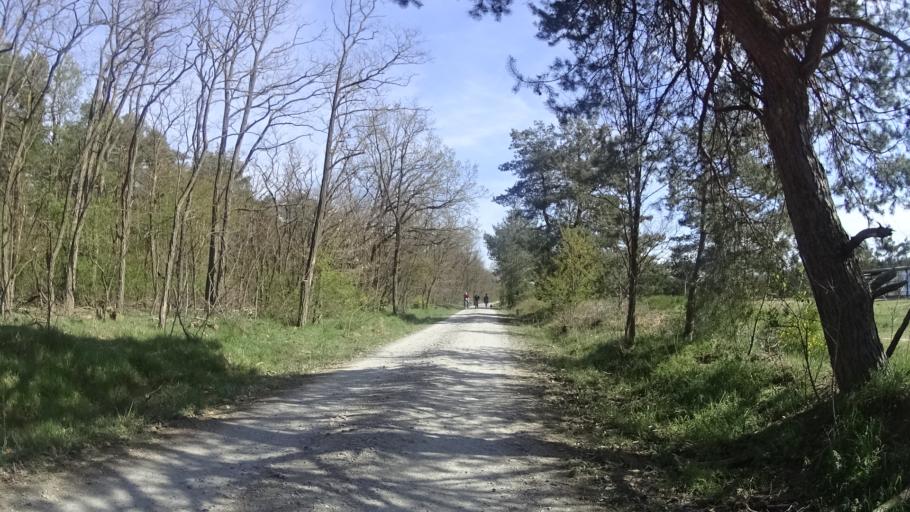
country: DE
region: Hesse
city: Lampertheim
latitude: 49.5812
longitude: 8.5079
